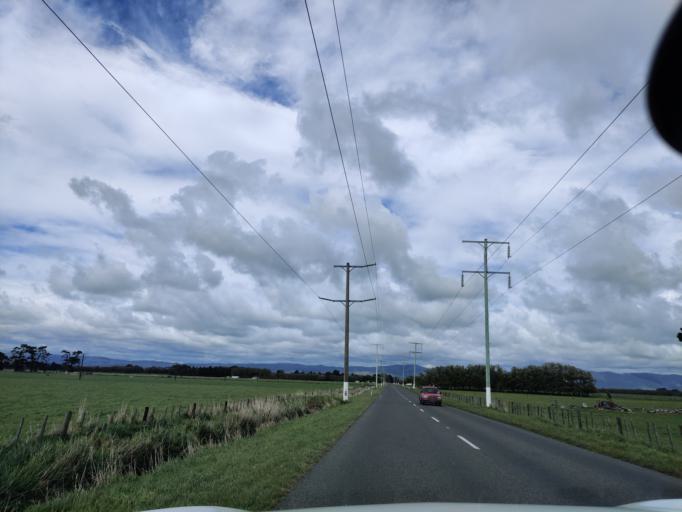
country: NZ
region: Manawatu-Wanganui
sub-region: Palmerston North City
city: Palmerston North
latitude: -40.3559
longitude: 175.5413
